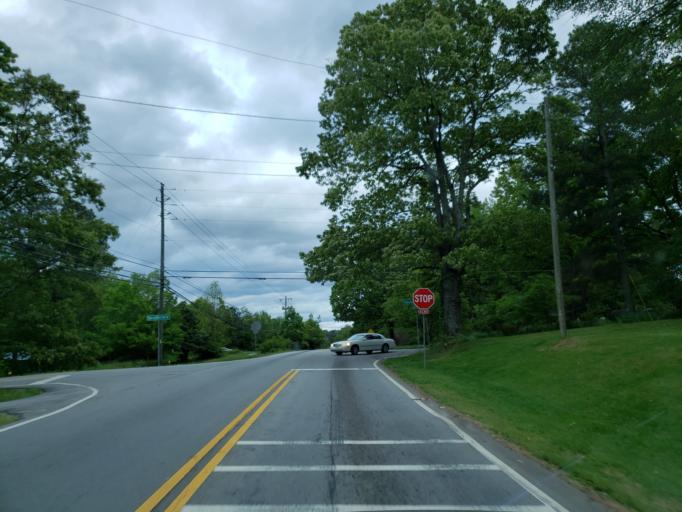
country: US
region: Georgia
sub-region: Paulding County
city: Dallas
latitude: 33.8679
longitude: -84.8254
